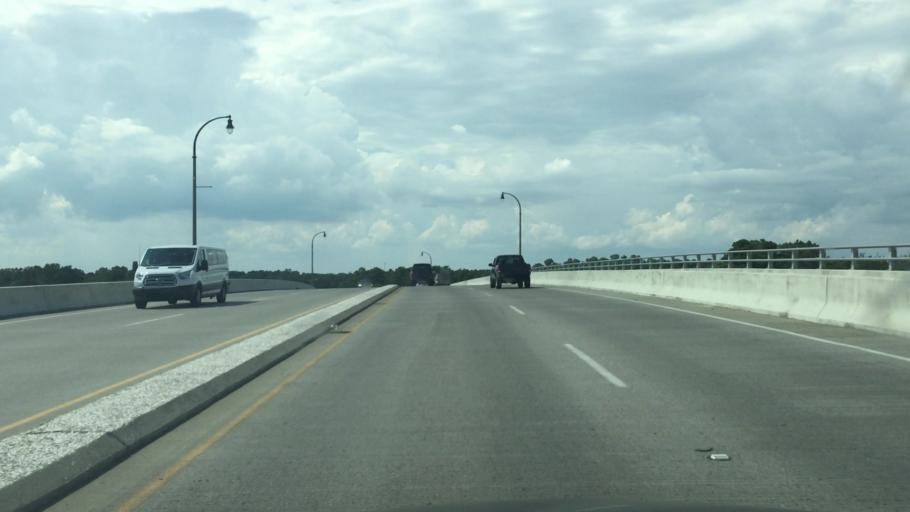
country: US
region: South Carolina
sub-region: Horry County
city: North Myrtle Beach
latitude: 33.8336
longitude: -78.6840
